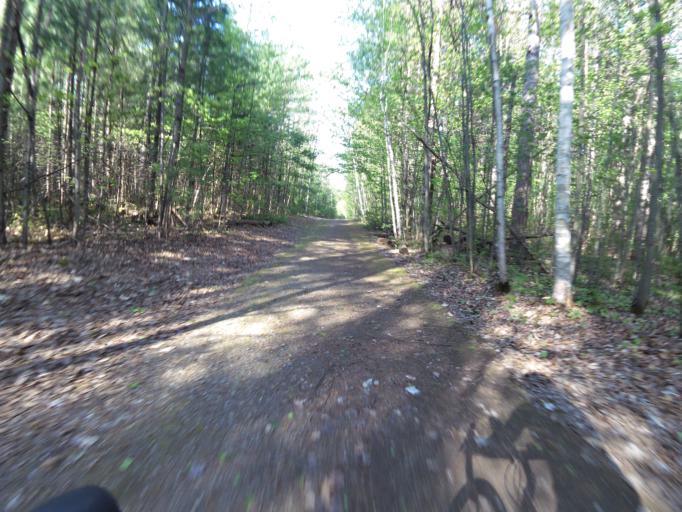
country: CA
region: Ontario
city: Bells Corners
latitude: 45.3269
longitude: -75.7398
